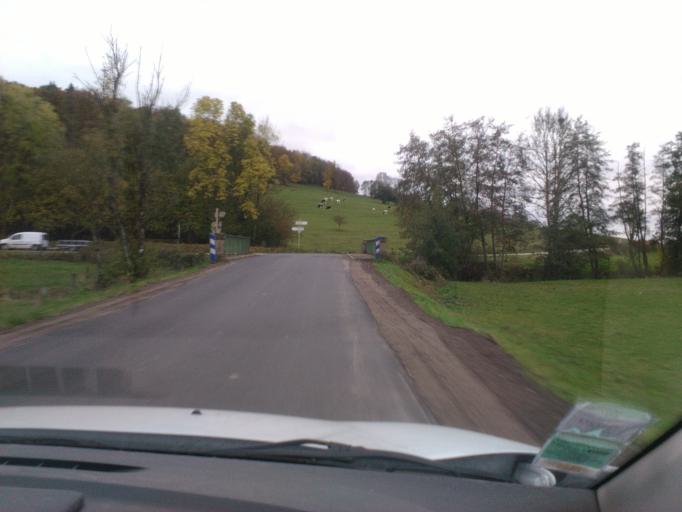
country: FR
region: Lorraine
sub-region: Departement des Vosges
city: Mirecourt
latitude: 48.2757
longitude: 6.2335
